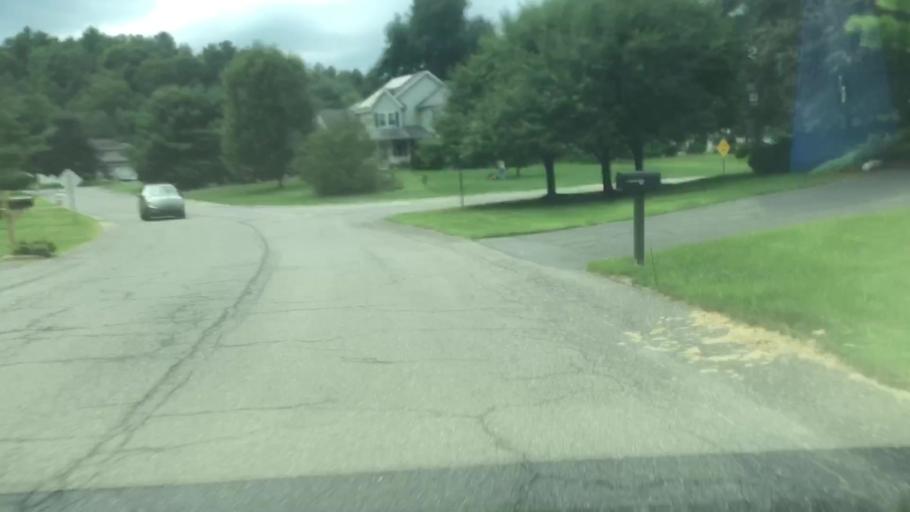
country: US
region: New York
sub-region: Albany County
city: Westmere
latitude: 42.7316
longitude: -73.9209
